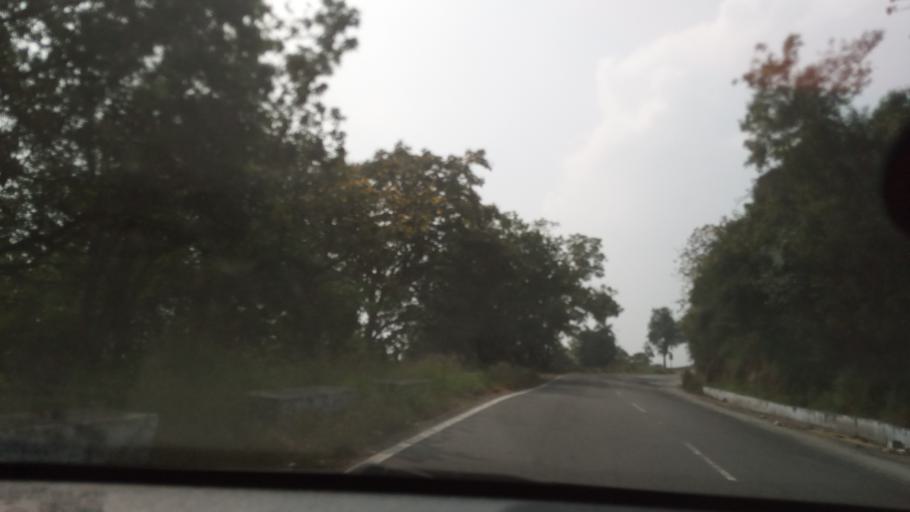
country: IN
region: Tamil Nadu
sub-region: Erode
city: Sathyamangalam
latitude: 11.5944
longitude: 77.1270
